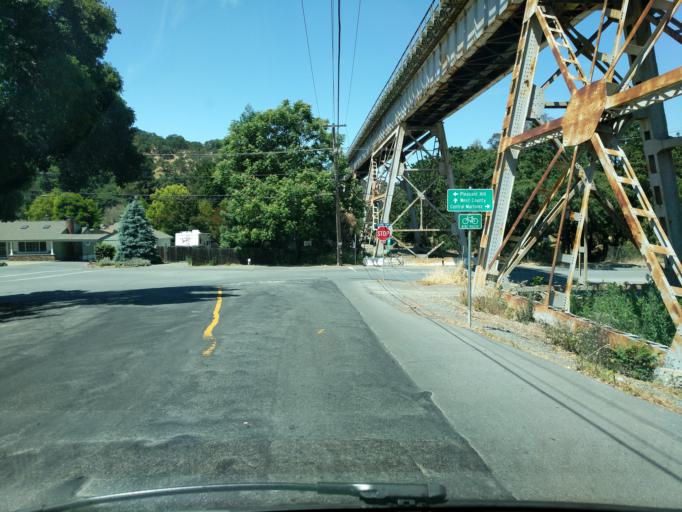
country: US
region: California
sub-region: Contra Costa County
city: Mountain View
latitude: 37.9908
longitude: -122.1256
